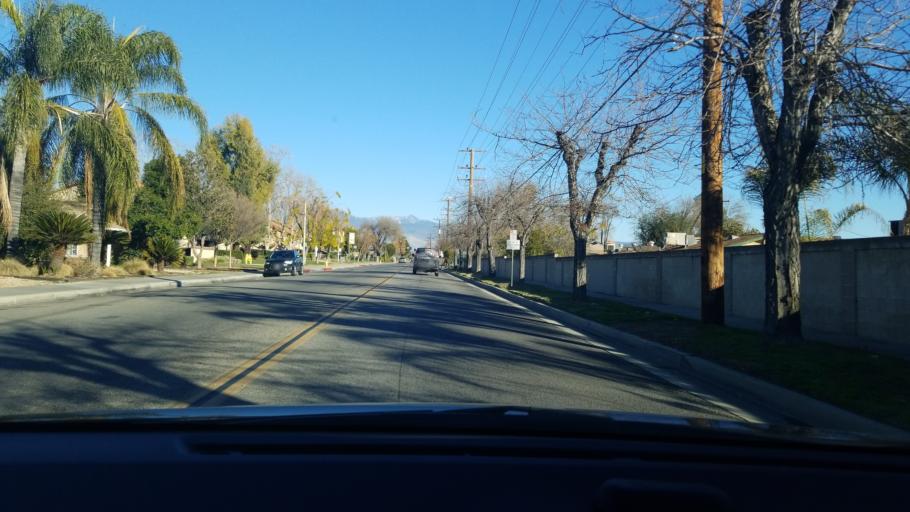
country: US
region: California
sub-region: Riverside County
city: Hemet
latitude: 33.7510
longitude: -117.0015
